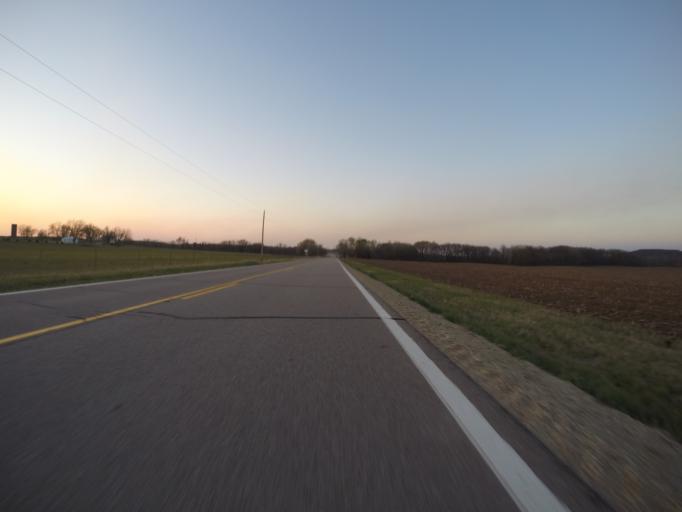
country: US
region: Kansas
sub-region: Riley County
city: Ogden
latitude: 39.0923
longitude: -96.6518
